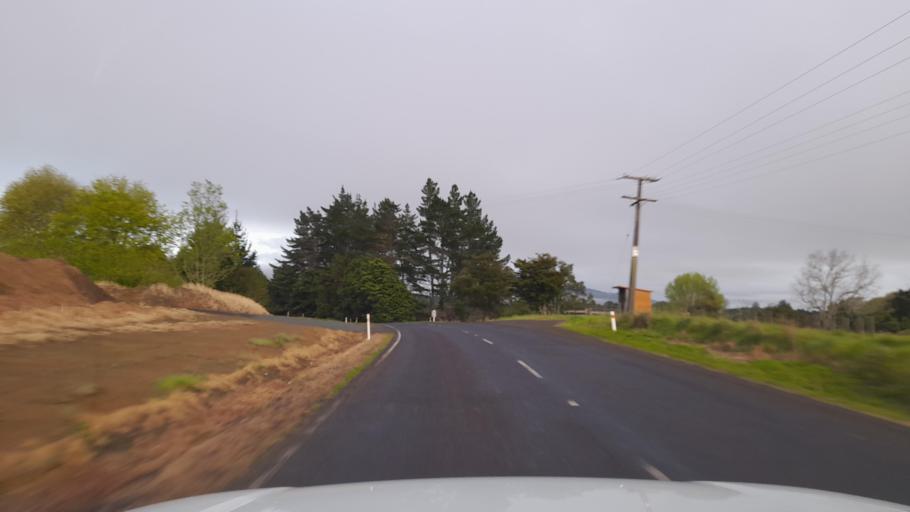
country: NZ
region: Northland
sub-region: Kaipara District
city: Dargaville
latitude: -35.7070
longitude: 173.9343
